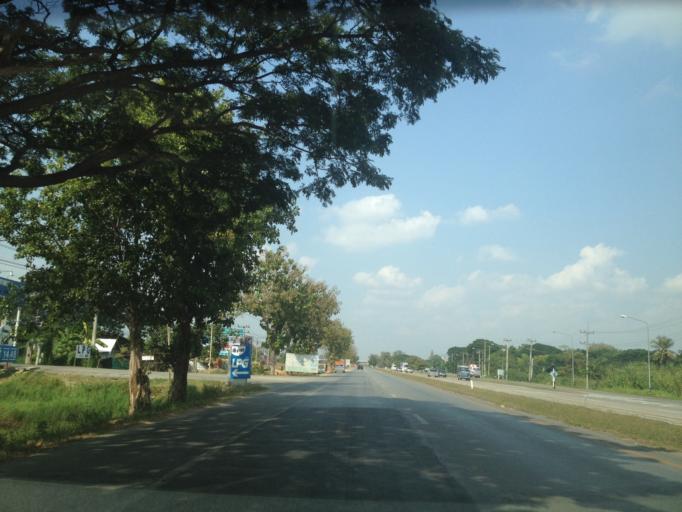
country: TH
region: Chiang Mai
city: Saraphi
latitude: 18.7280
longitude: 99.0397
